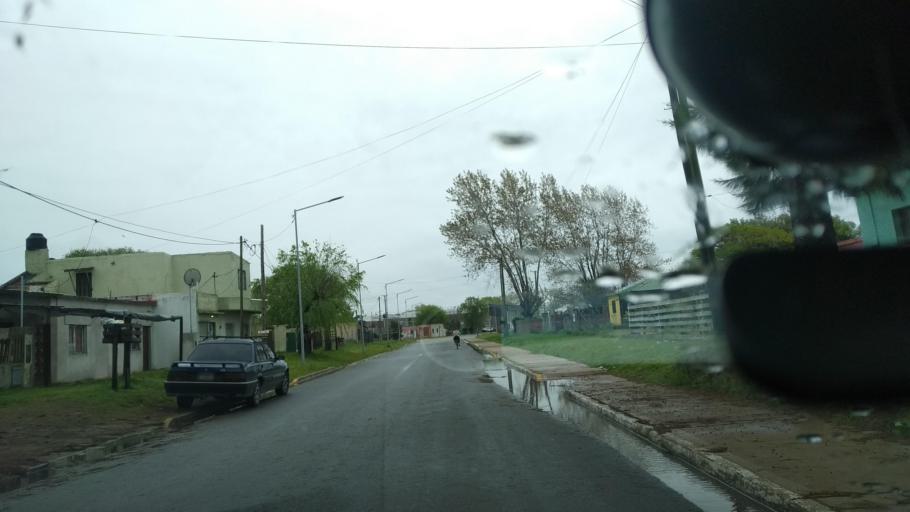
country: AR
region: Buenos Aires
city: Mar del Tuyu
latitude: -36.5397
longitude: -56.7094
